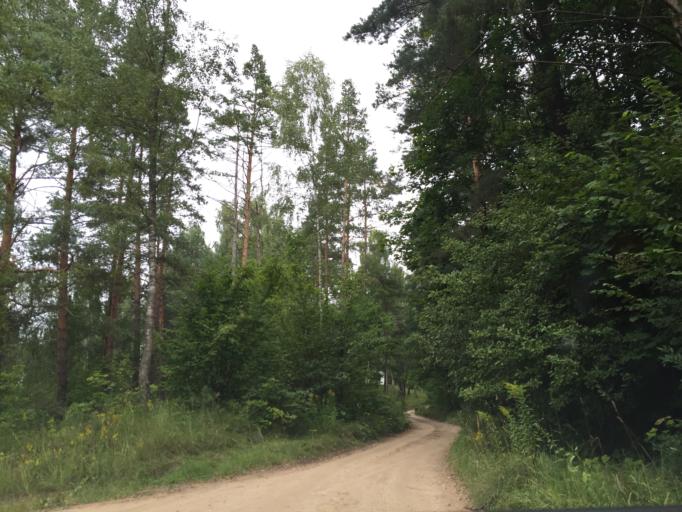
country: LV
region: Kegums
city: Kegums
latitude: 56.7491
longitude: 24.7096
